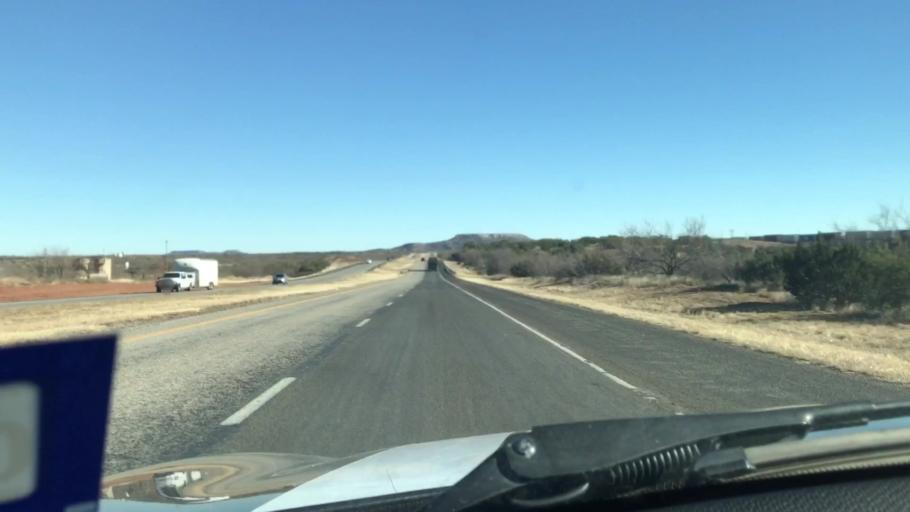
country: US
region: Texas
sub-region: Garza County
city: Post
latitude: 32.9847
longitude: -101.1254
